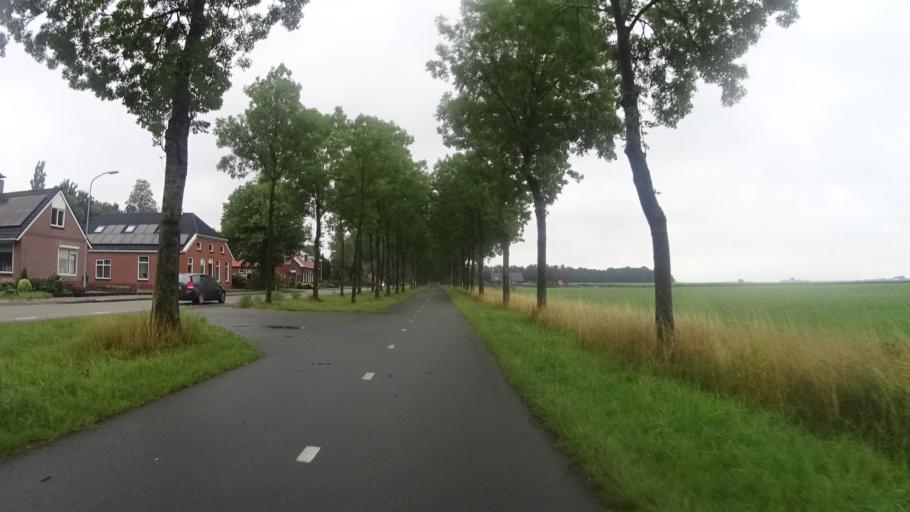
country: NL
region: Groningen
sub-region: Gemeente  Oldambt
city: Winschoten
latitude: 53.1653
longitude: 7.0862
